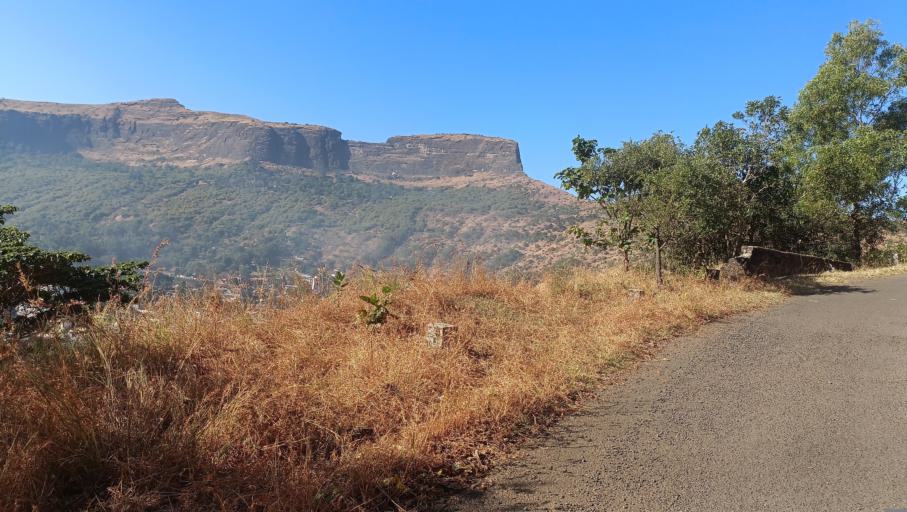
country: IN
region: Maharashtra
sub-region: Nashik Division
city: Trimbak
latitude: 19.9380
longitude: 73.5285
